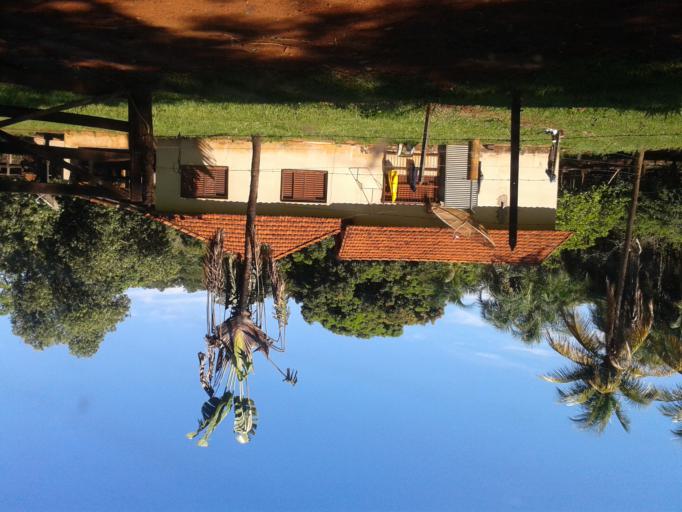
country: BR
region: Minas Gerais
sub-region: Capinopolis
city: Capinopolis
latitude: -18.6748
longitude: -49.5857
